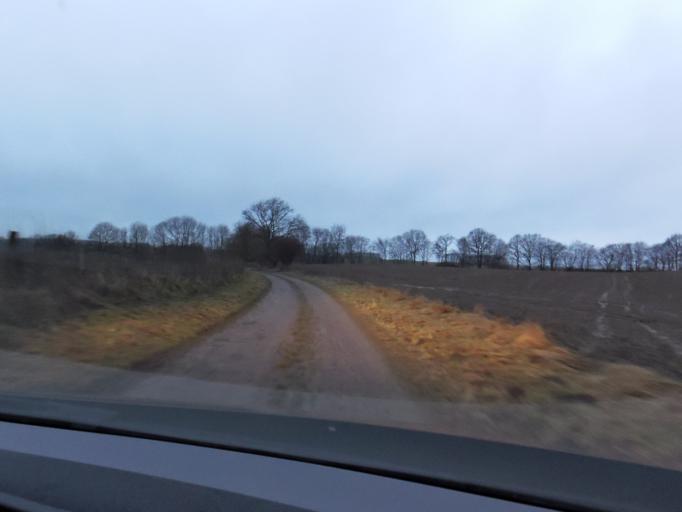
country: DE
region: Mecklenburg-Vorpommern
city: Roggendorf
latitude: 53.6826
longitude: 10.9811
